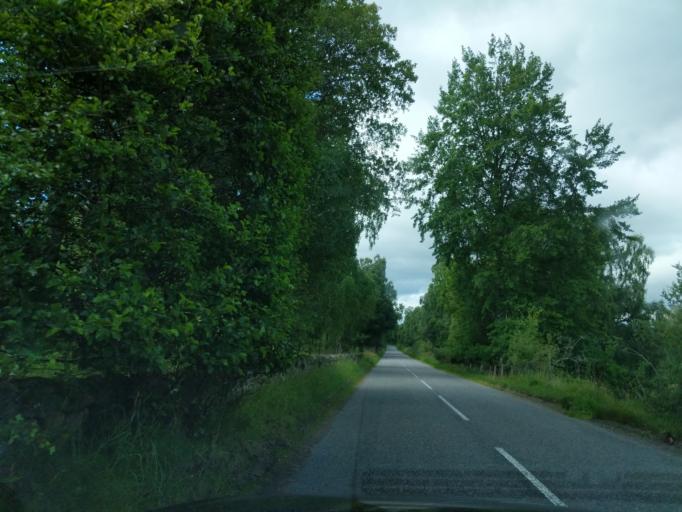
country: GB
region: Scotland
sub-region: Aberdeenshire
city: Aboyne
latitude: 57.0688
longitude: -2.8995
